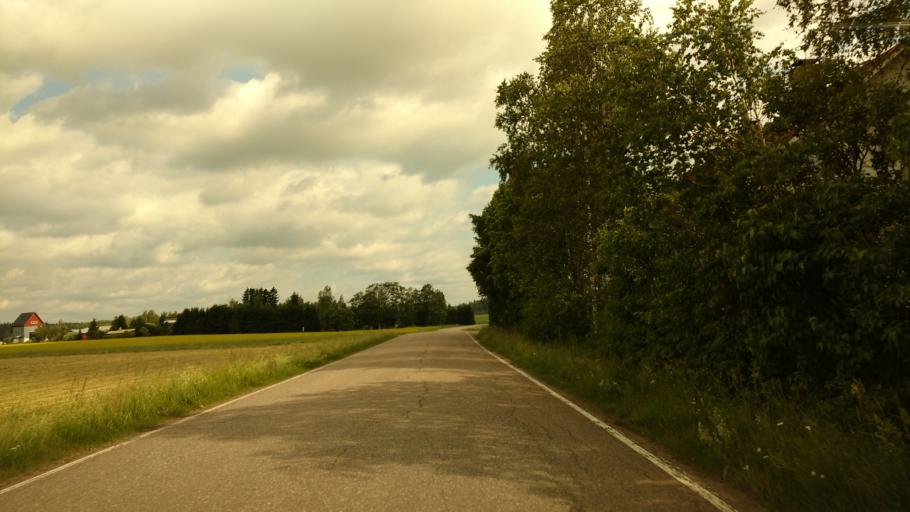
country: FI
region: Haeme
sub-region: Forssa
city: Ypaejae
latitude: 60.7858
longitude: 23.2706
